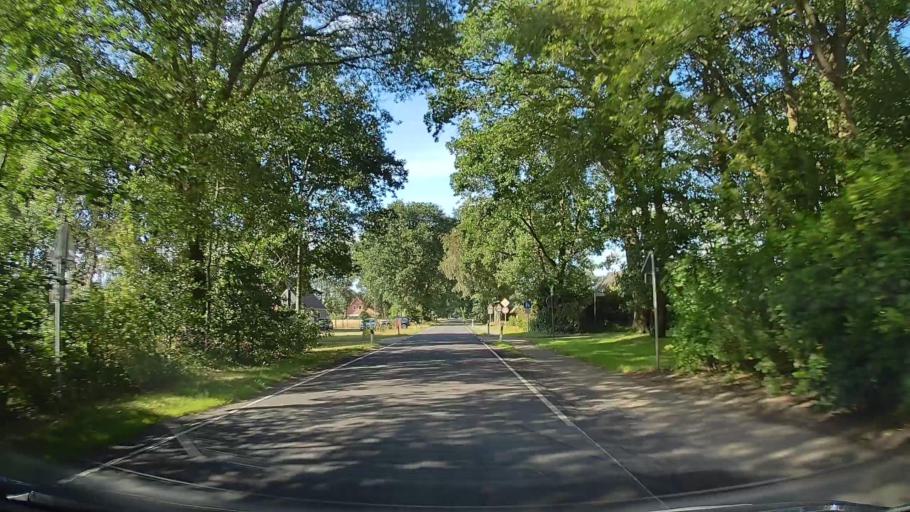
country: DE
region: Lower Saxony
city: Molbergen
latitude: 52.9306
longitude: 7.8936
